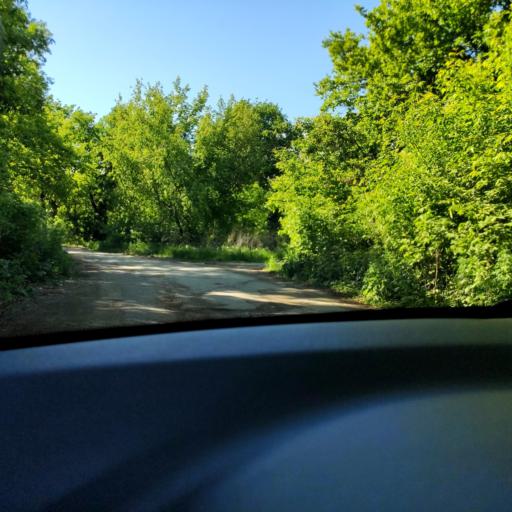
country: RU
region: Samara
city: Samara
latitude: 53.2242
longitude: 50.1632
